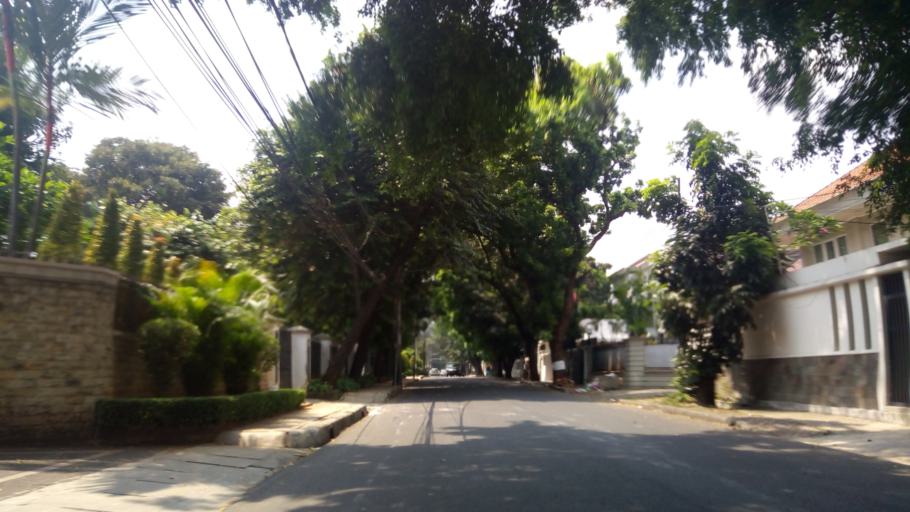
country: ID
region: Jakarta Raya
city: Jakarta
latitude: -6.2009
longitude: 106.8292
